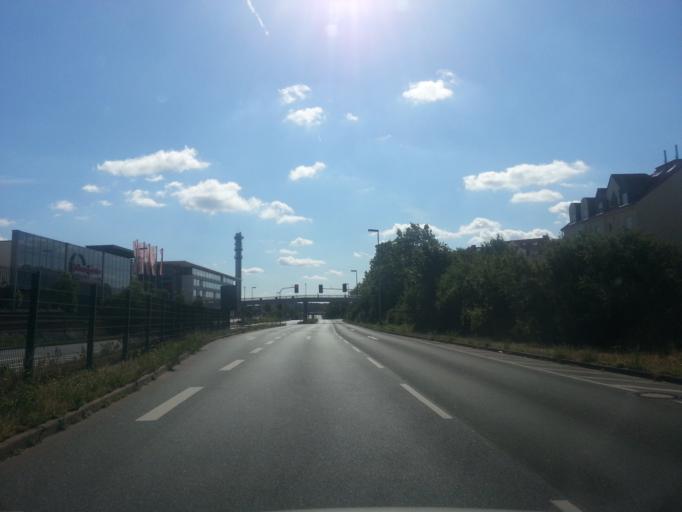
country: DE
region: Hesse
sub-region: Regierungsbezirk Darmstadt
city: Dietzenbach
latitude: 50.0173
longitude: 8.7824
